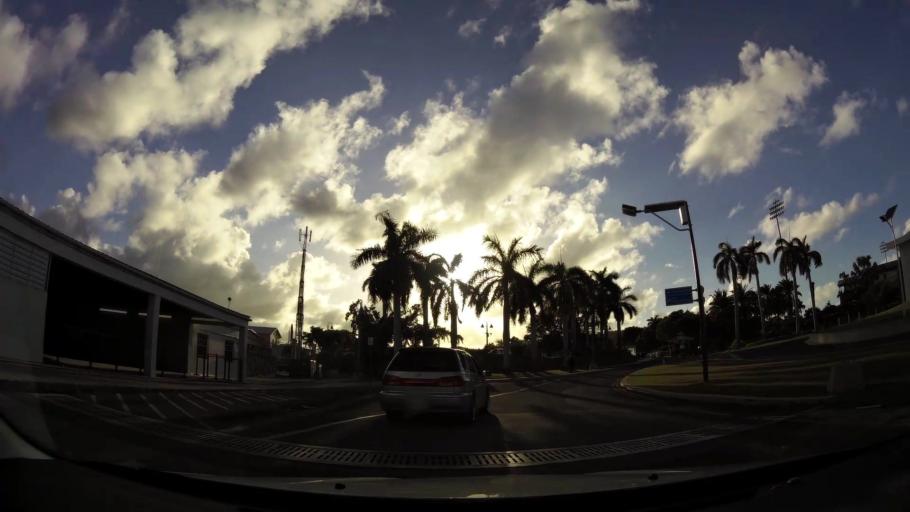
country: AG
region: Saint George
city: Piggotts
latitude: 17.1402
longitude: -61.7931
